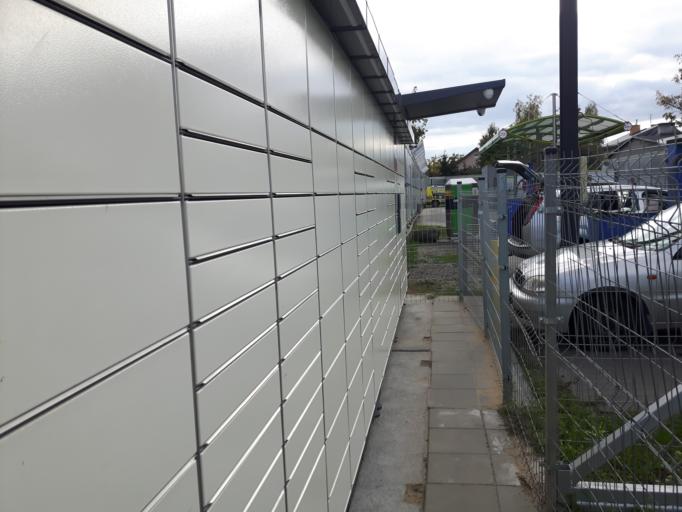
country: PL
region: Masovian Voivodeship
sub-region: Powiat wolominski
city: Zabki
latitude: 52.2838
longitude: 21.1154
